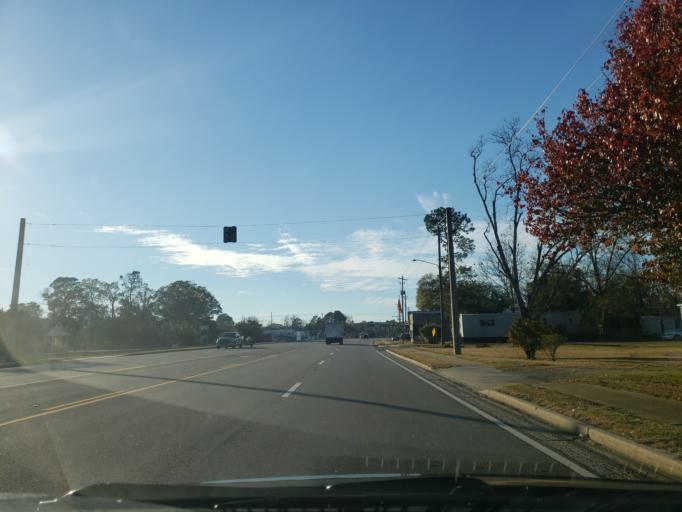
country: US
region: Georgia
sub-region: Atkinson County
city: Pearson
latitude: 31.2973
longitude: -82.8489
